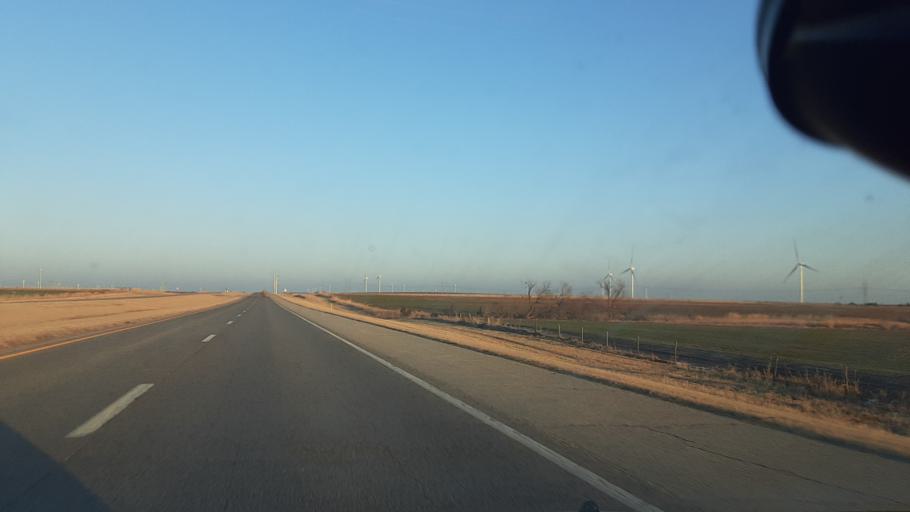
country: US
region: Oklahoma
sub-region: Noble County
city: Perry
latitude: 36.3975
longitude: -97.4916
